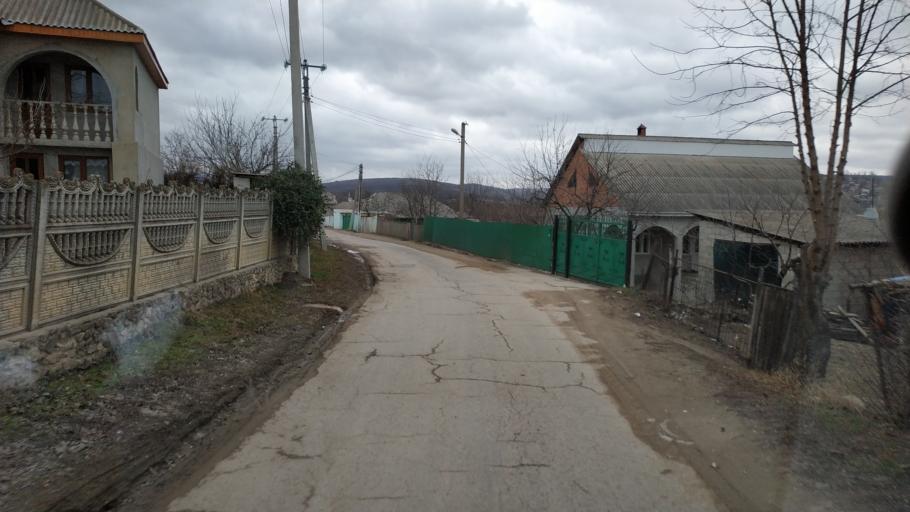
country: MD
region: Calarasi
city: Calarasi
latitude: 47.2424
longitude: 28.3074
